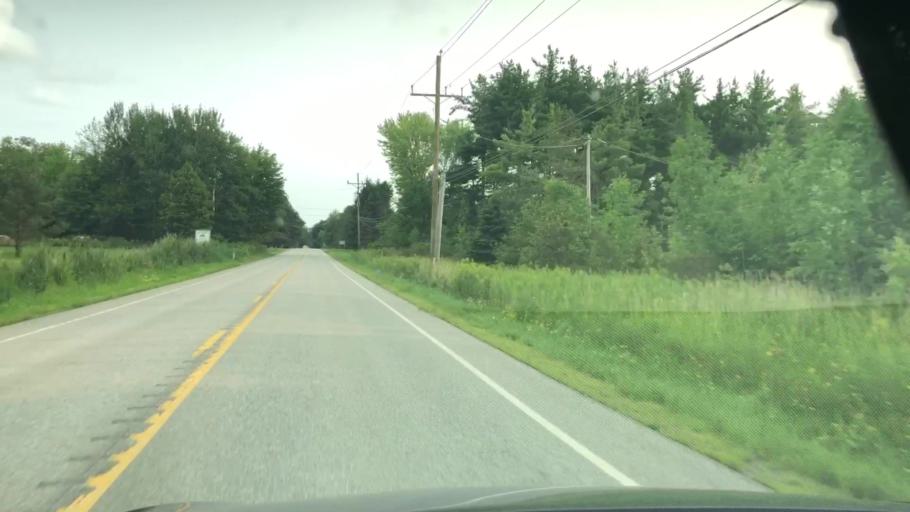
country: US
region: Pennsylvania
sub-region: Erie County
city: Union City
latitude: 41.9287
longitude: -79.8436
